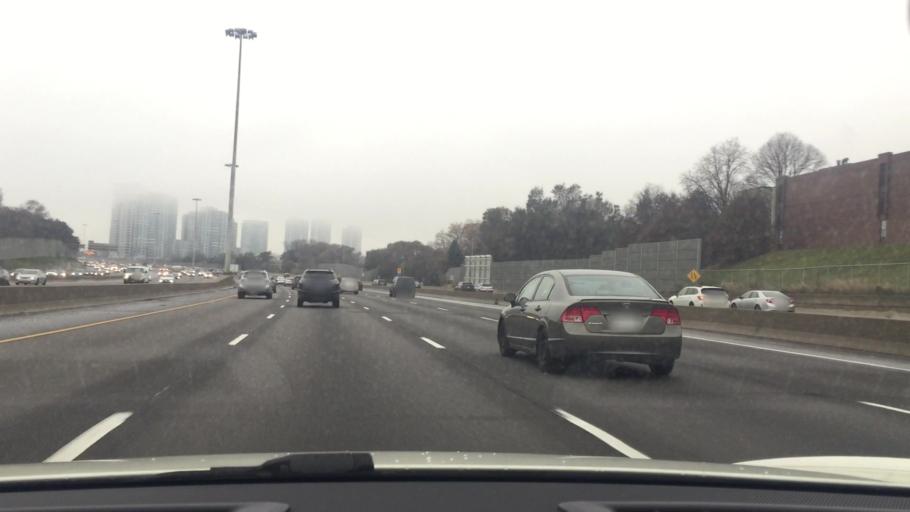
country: CA
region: Ontario
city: Willowdale
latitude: 43.7631
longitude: -79.3929
